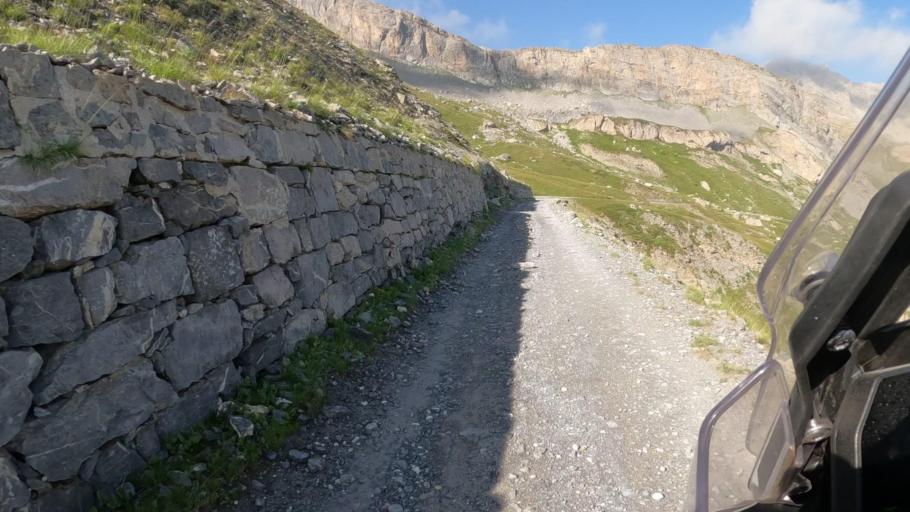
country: IT
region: Piedmont
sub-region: Provincia di Cuneo
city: Pietraporzio
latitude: 44.3856
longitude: 7.0391
